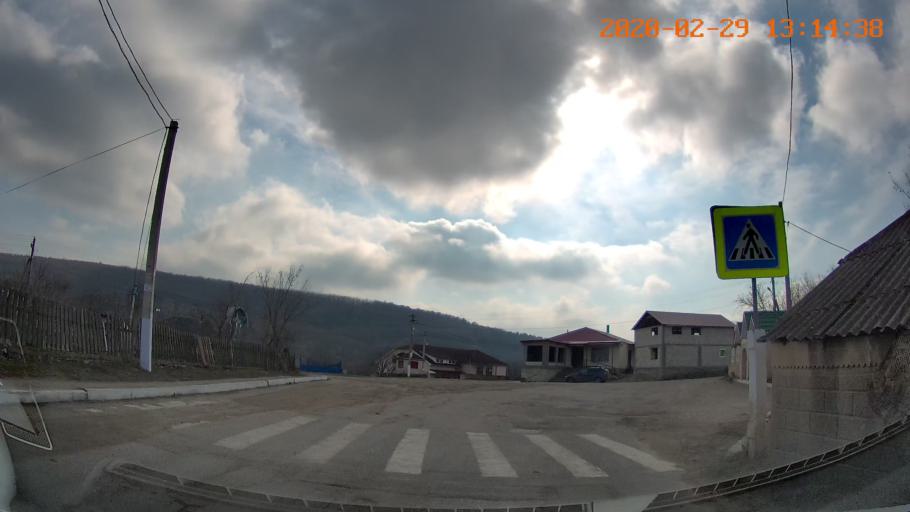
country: MD
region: Telenesti
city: Camenca
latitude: 48.0117
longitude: 28.6760
